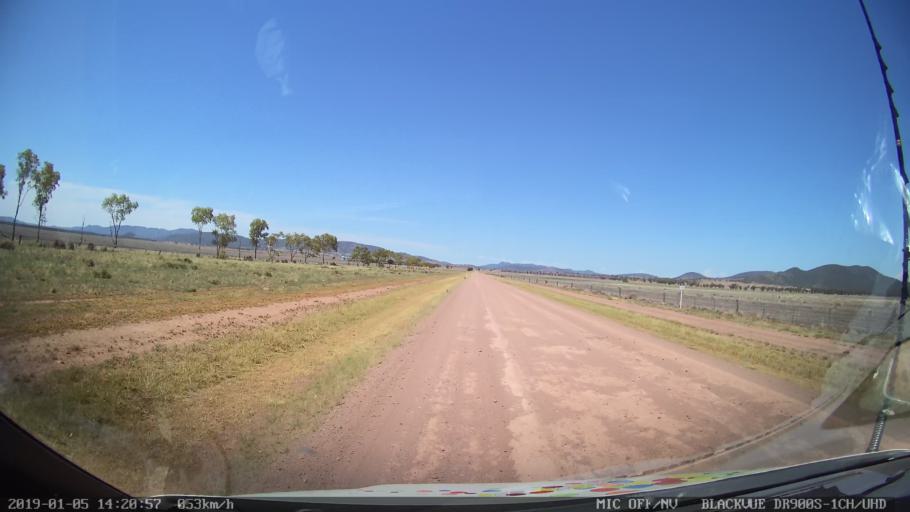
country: AU
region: New South Wales
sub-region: Liverpool Plains
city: Quirindi
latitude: -31.2478
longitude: 150.5094
